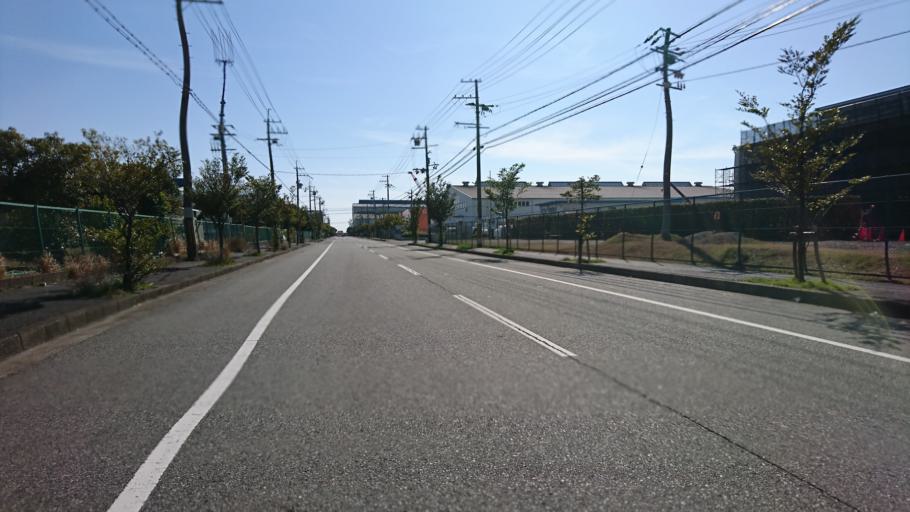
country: JP
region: Hyogo
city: Kakogawacho-honmachi
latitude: 34.7003
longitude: 134.8492
